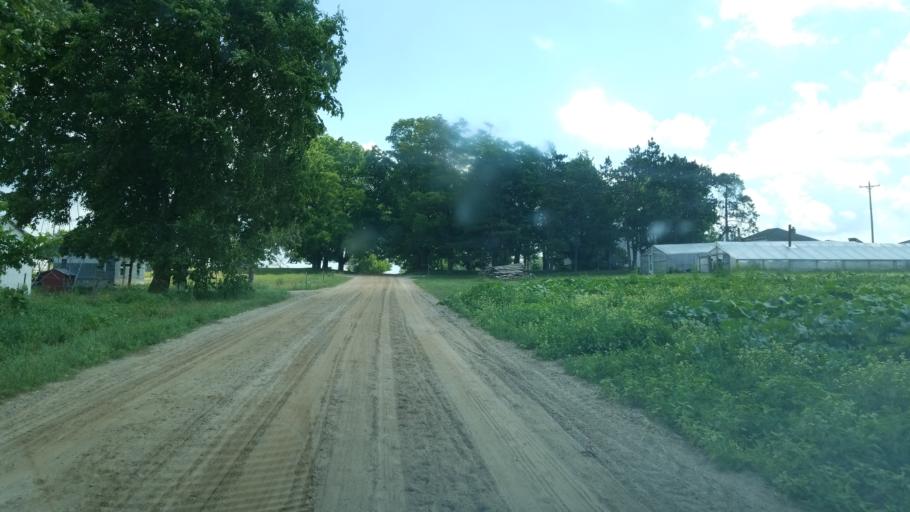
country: US
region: Michigan
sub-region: Mecosta County
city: Canadian Lakes
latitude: 43.5693
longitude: -85.3781
